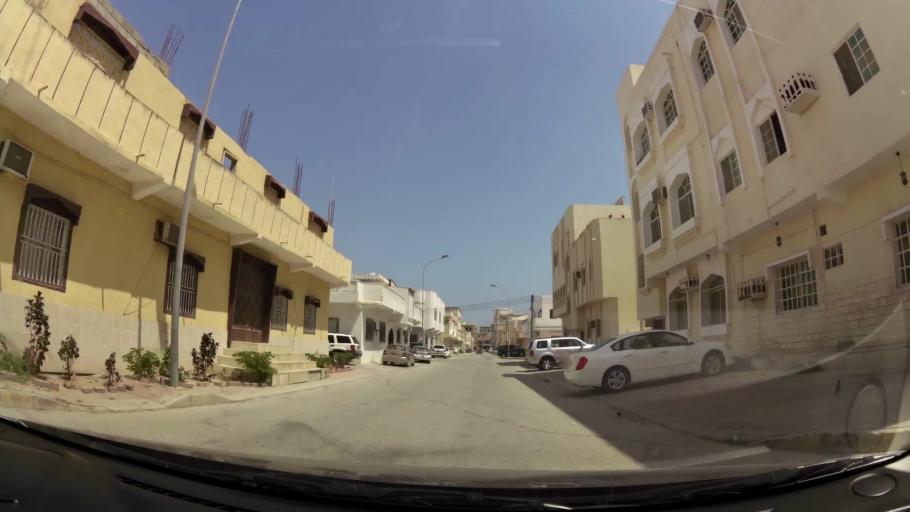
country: OM
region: Zufar
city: Salalah
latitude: 17.0203
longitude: 54.0869
